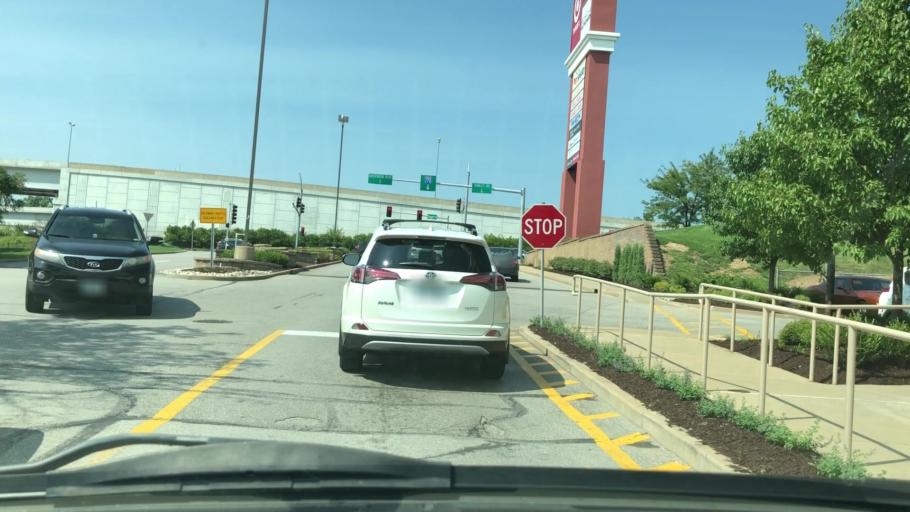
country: US
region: Missouri
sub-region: Saint Louis County
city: Brentwood
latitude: 38.6281
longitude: -90.3416
